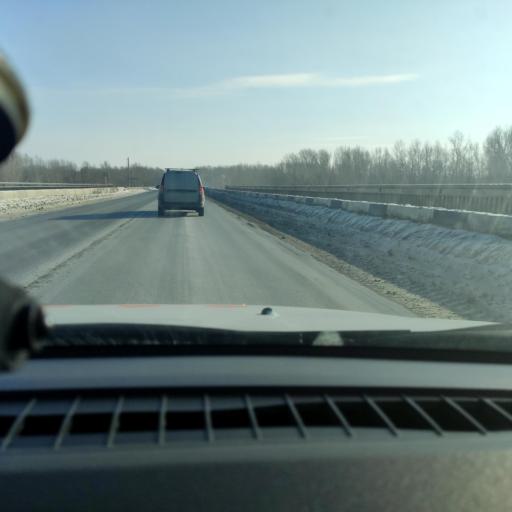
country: RU
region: Samara
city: Smyshlyayevka
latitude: 53.2329
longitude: 50.4889
